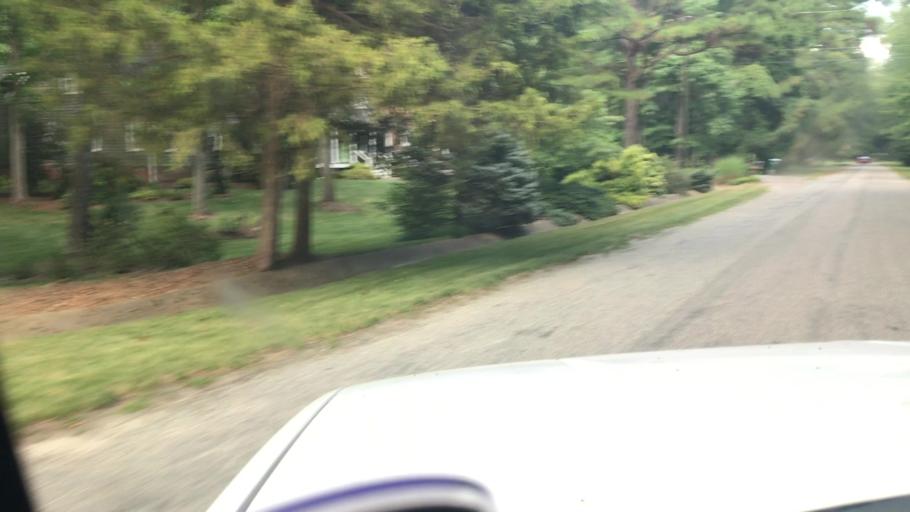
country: US
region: Virginia
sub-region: Henrico County
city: Short Pump
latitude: 37.6066
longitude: -77.7163
